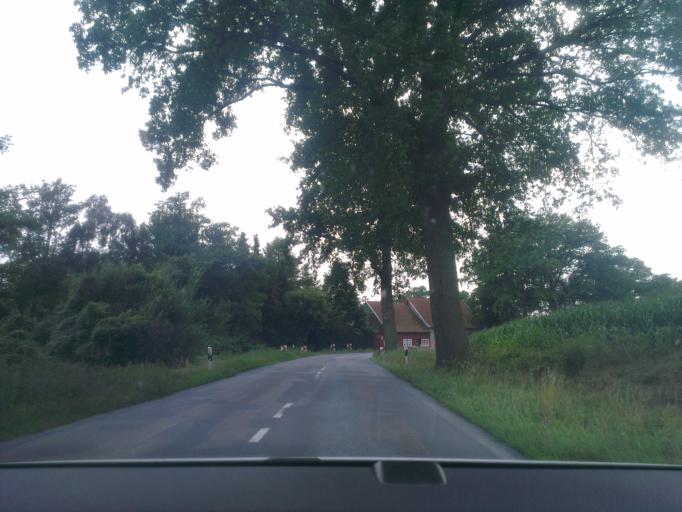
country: DE
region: Lower Saxony
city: Menslage
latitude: 52.6405
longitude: 7.8056
